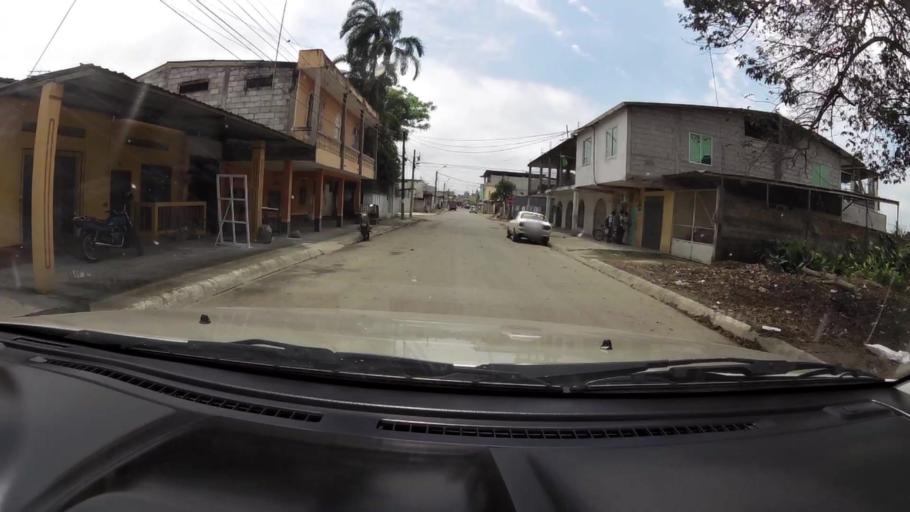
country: EC
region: El Oro
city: Pasaje
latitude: -3.2416
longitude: -79.8266
